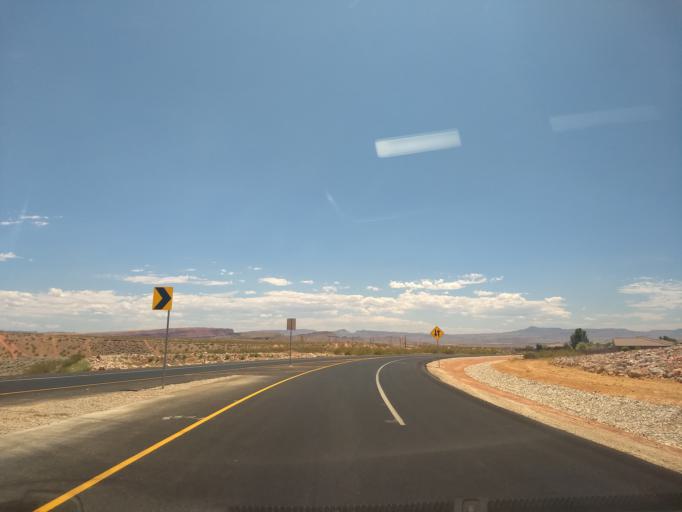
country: US
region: Utah
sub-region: Washington County
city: Washington
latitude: 37.1582
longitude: -113.5198
